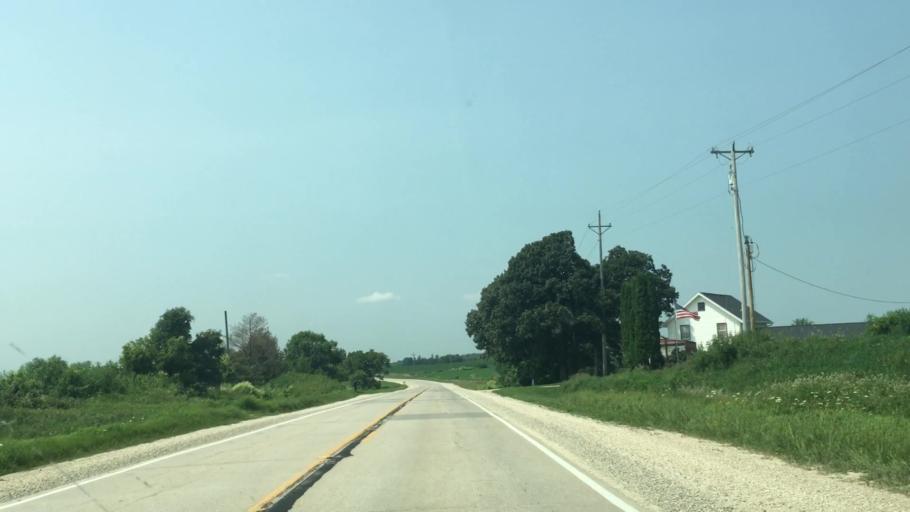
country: US
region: Iowa
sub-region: Fayette County
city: West Union
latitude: 43.0913
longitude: -91.8549
